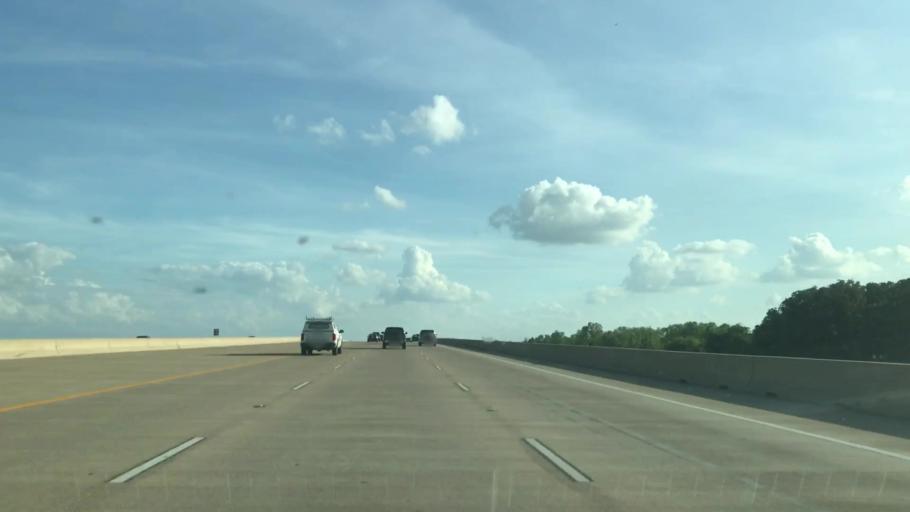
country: US
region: Texas
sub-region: Dallas County
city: Grand Prairie
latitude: 32.8038
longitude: -97.0186
